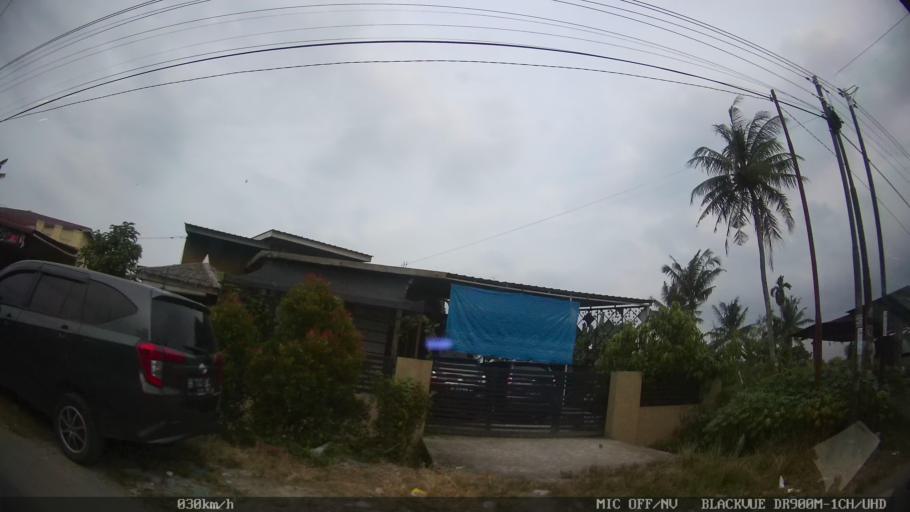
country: ID
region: North Sumatra
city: Sunggal
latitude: 3.5629
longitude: 98.5972
